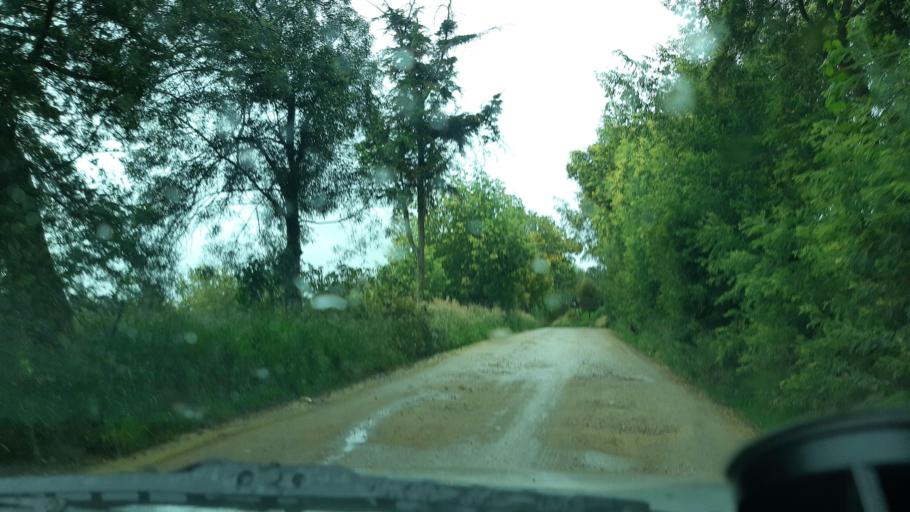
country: CO
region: Cundinamarca
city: Villapinzon
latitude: 5.2164
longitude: -73.5725
